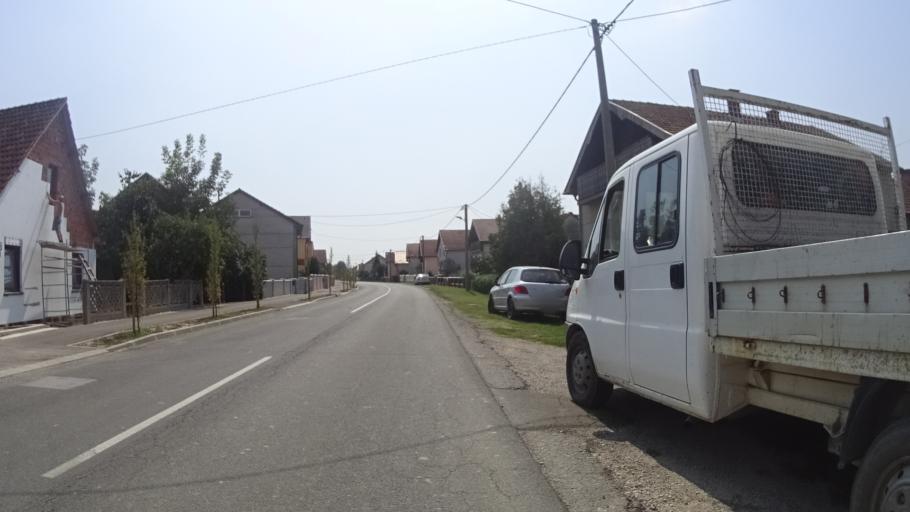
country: HR
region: Medimurska
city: Hodosan
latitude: 46.4004
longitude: 16.6343
